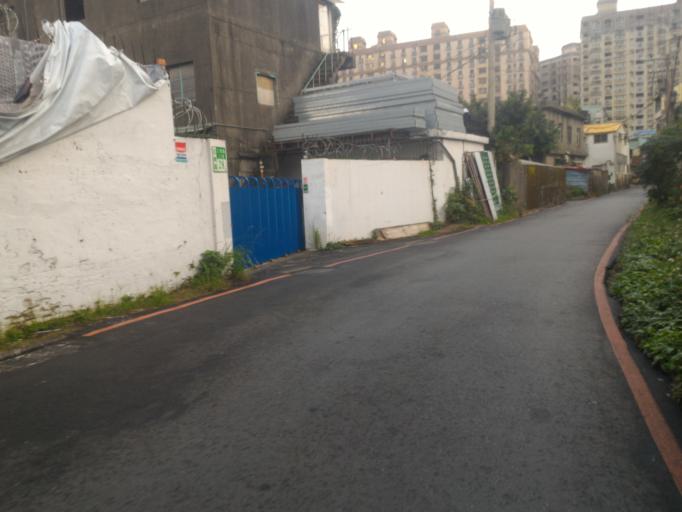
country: TW
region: Taiwan
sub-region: Taoyuan
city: Taoyuan
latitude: 24.9425
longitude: 121.3807
